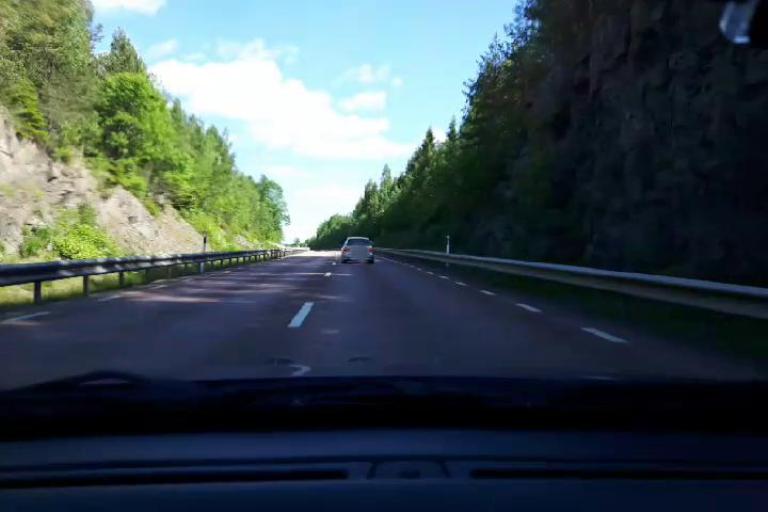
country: SE
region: Gaevleborg
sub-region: Hudiksvalls Kommun
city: Sorforsa
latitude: 61.7410
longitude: 16.8641
